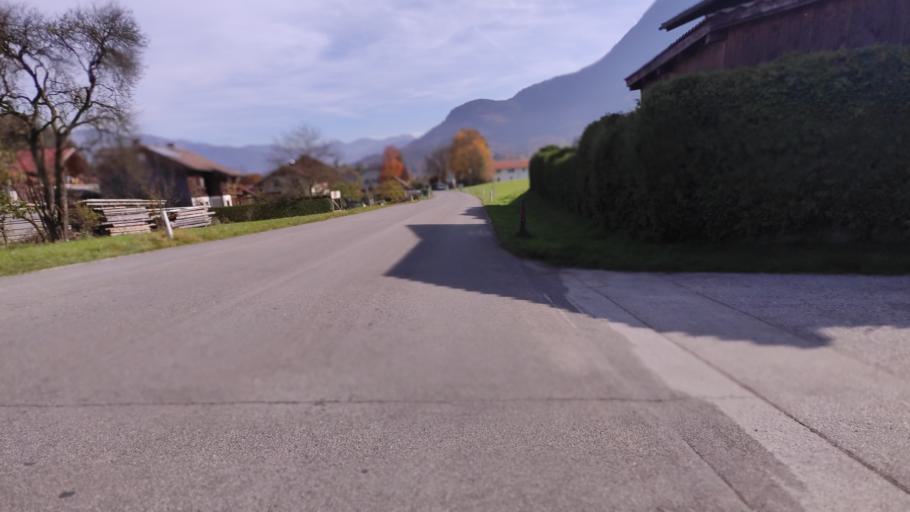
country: AT
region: Salzburg
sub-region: Politischer Bezirk Salzburg-Umgebung
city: Strobl
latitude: 47.7158
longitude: 13.5330
